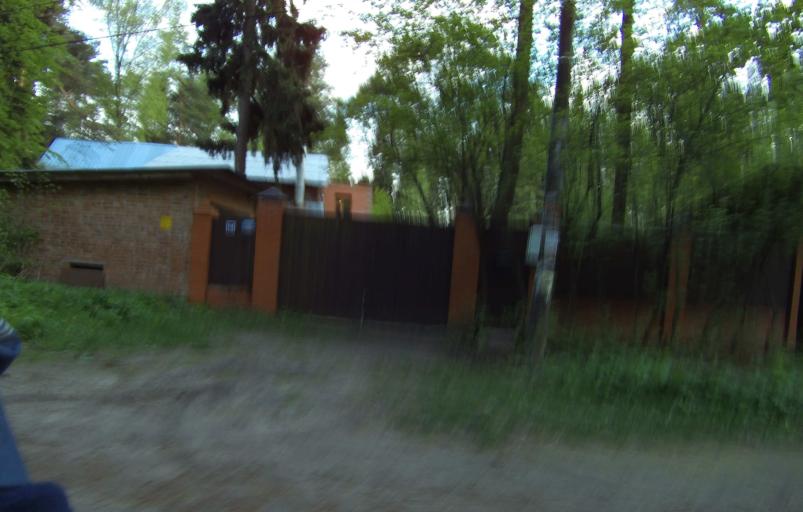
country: RU
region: Moskovskaya
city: Kratovo
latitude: 55.5975
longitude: 38.1588
